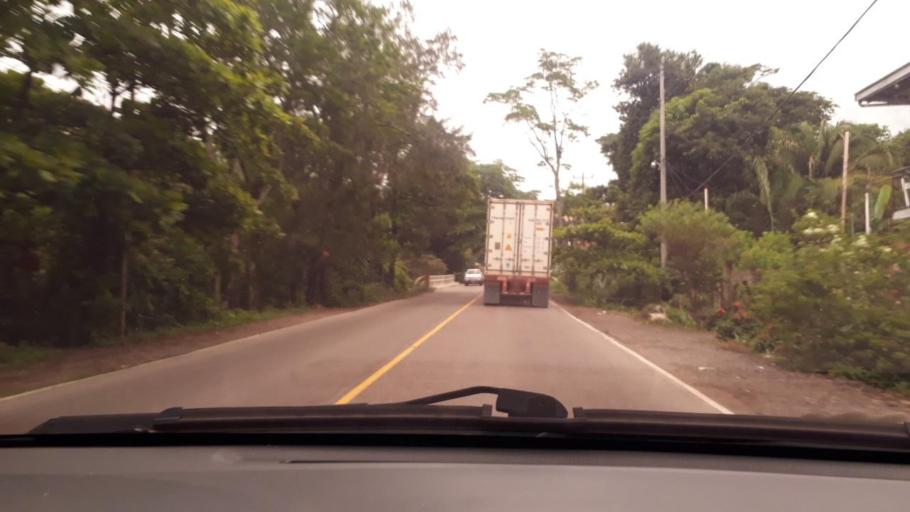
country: GT
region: Chiquimula
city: Quezaltepeque
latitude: 14.6214
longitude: -89.4463
